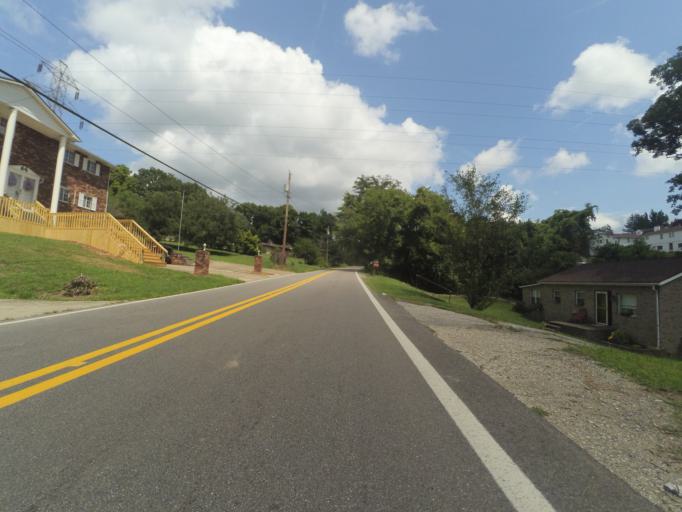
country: US
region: West Virginia
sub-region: Cabell County
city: Pea Ridge
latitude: 38.4119
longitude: -82.3550
